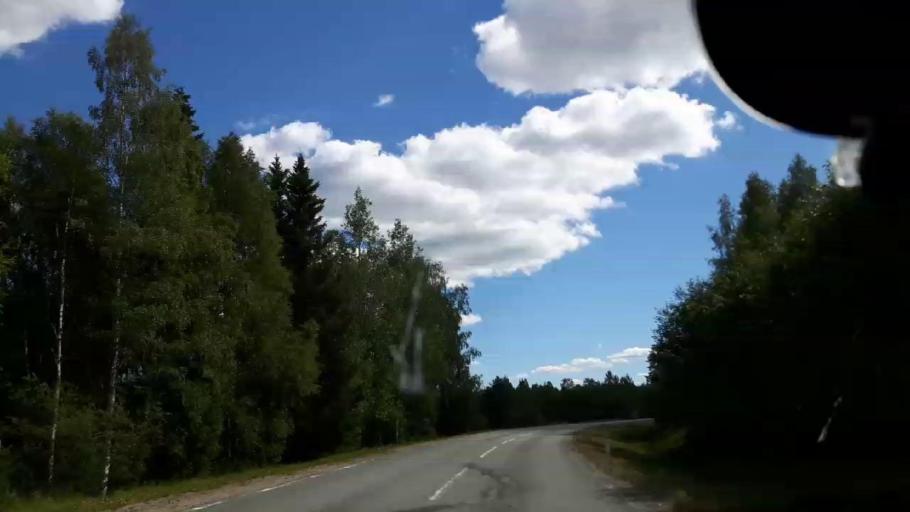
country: SE
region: Jaemtland
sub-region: Ragunda Kommun
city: Hammarstrand
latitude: 62.8307
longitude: 16.1835
